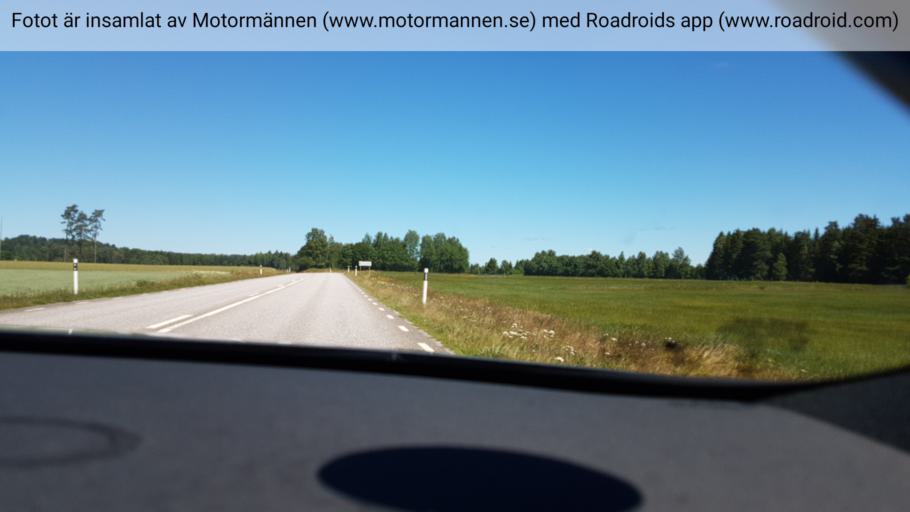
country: SE
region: Vaestra Goetaland
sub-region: Ulricehamns Kommun
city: Ulricehamn
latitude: 57.8730
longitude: 13.4329
